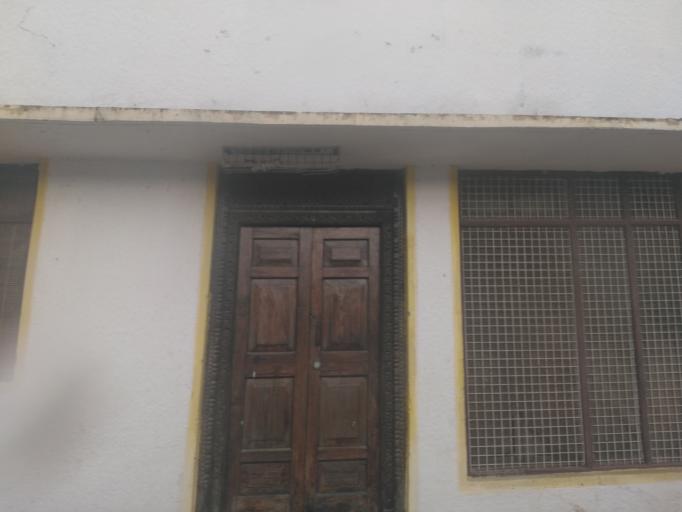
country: TZ
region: Zanzibar Urban/West
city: Zanzibar
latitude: -6.1659
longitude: 39.1977
